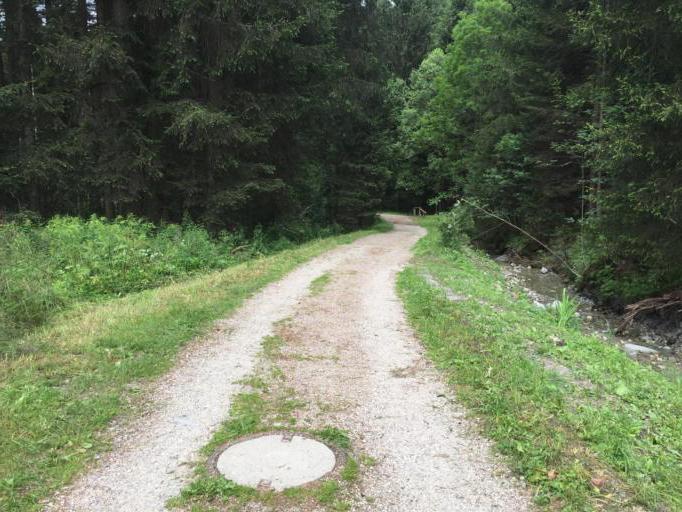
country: IT
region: Trentino-Alto Adige
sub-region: Bolzano
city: Falzes
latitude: 46.8082
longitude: 11.8745
